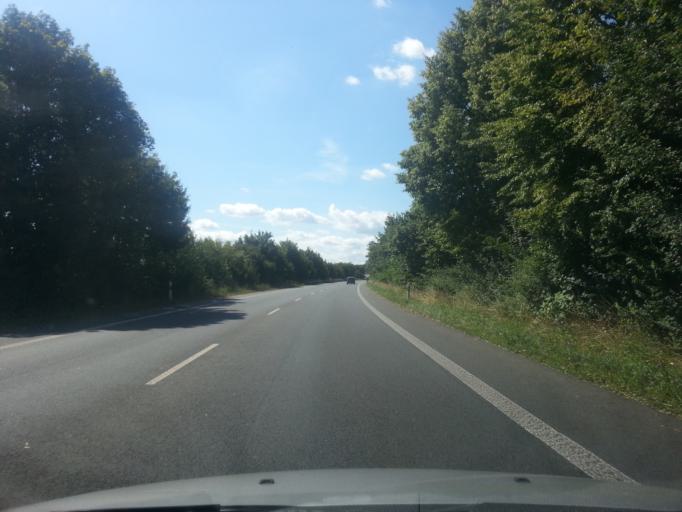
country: DE
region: Hesse
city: Gross-Umstadt
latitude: 49.8685
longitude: 8.9154
